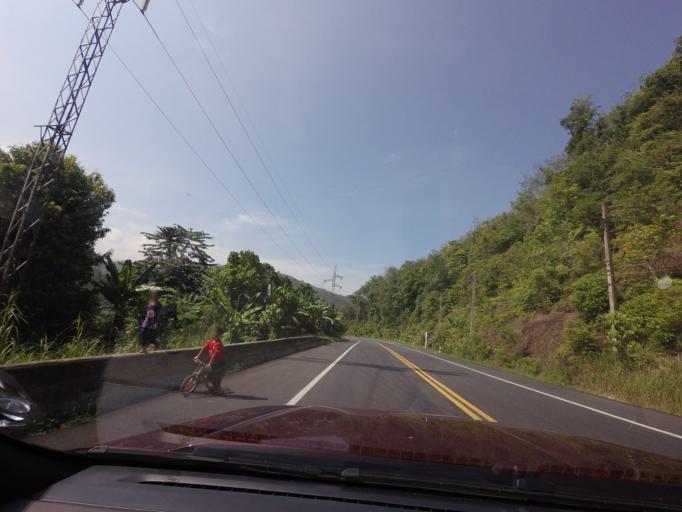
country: TH
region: Yala
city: Than To
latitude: 5.9784
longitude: 101.2000
